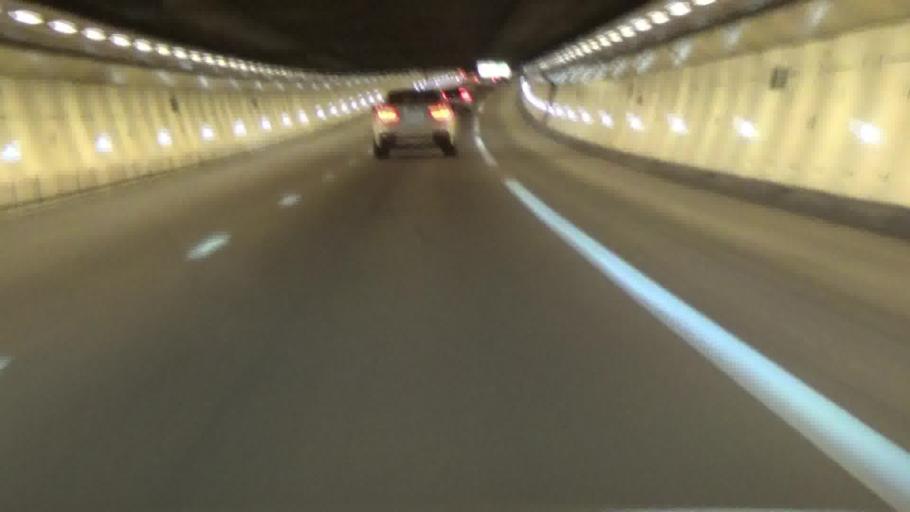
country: FR
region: Ile-de-France
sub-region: Departement des Yvelines
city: Viroflay
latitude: 48.8156
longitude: 2.1577
